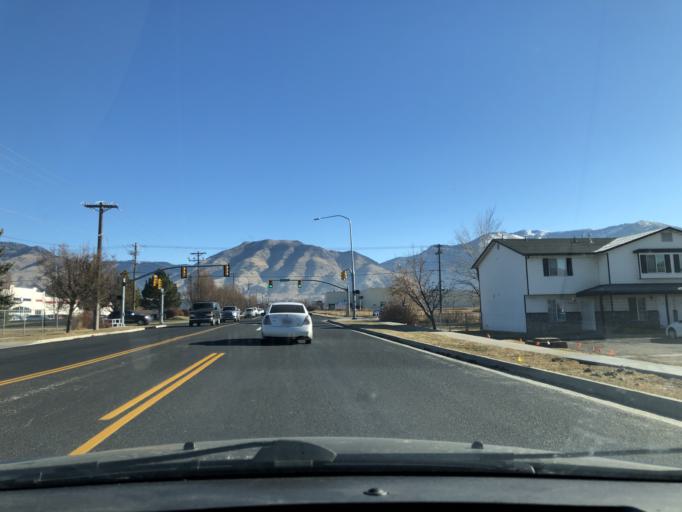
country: US
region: Utah
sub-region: Cache County
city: Logan
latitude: 41.7577
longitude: -111.8402
